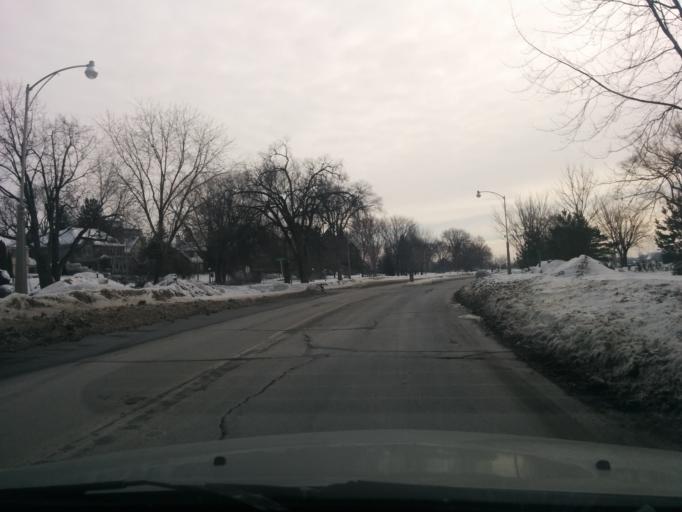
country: CA
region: Ontario
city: Ottawa
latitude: 45.3969
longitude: -75.7014
